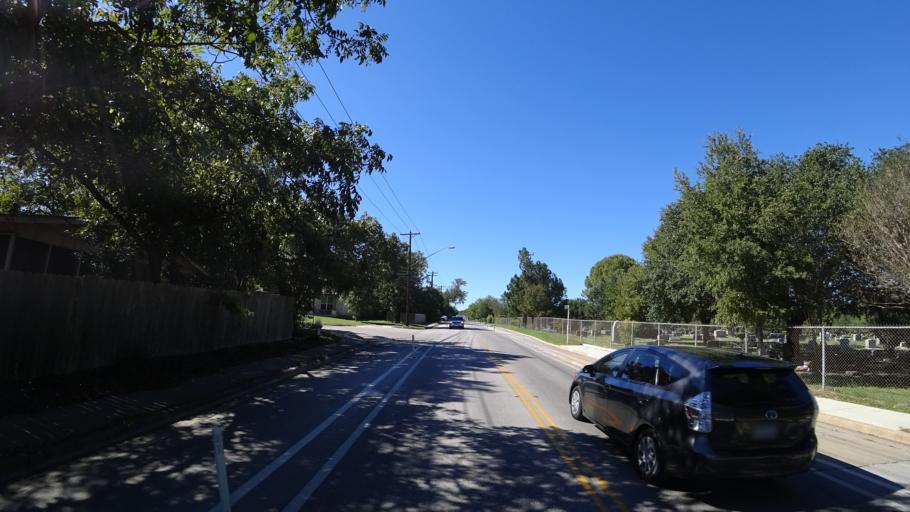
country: US
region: Texas
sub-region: Travis County
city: West Lake Hills
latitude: 30.3284
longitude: -97.7508
